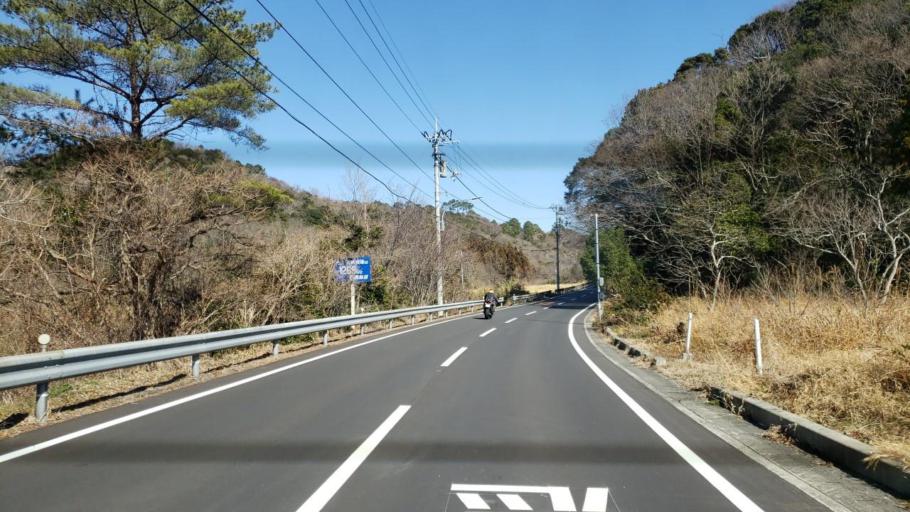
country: JP
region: Tokushima
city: Narutocho-mitsuishi
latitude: 34.2277
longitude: 134.5738
